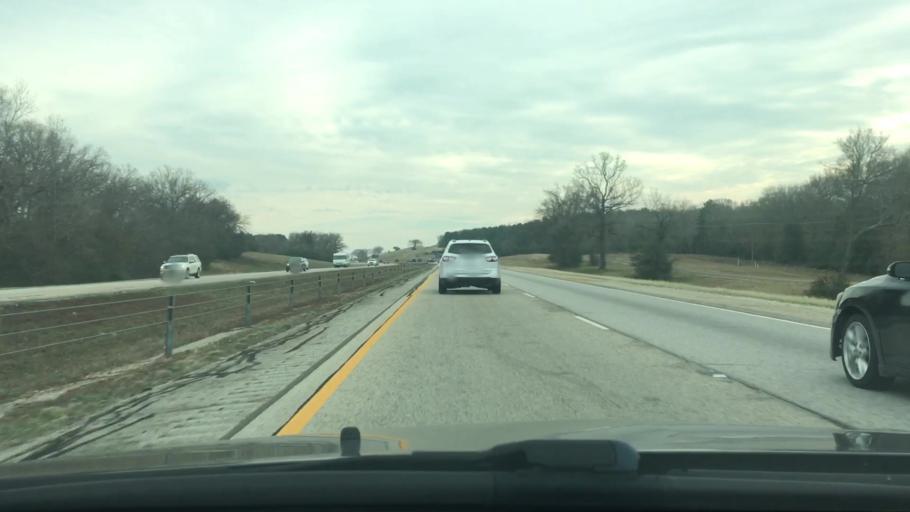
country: US
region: Texas
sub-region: Leon County
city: Centerville
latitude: 31.2974
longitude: -95.9990
